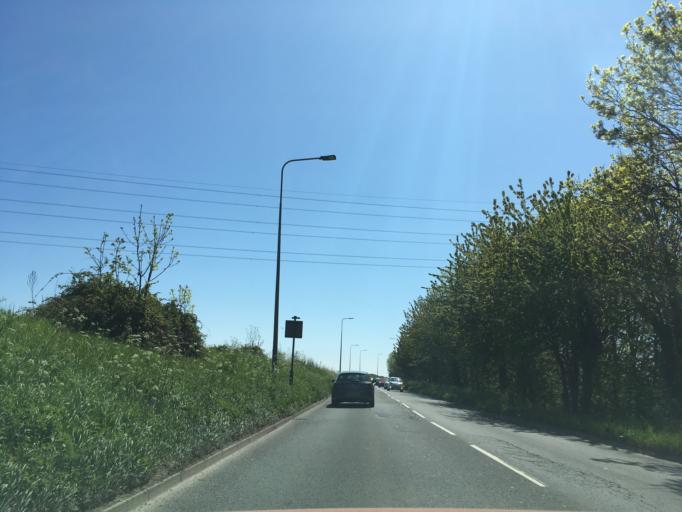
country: GB
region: Wales
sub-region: Cardiff
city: Cardiff
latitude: 51.4892
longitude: -3.1272
